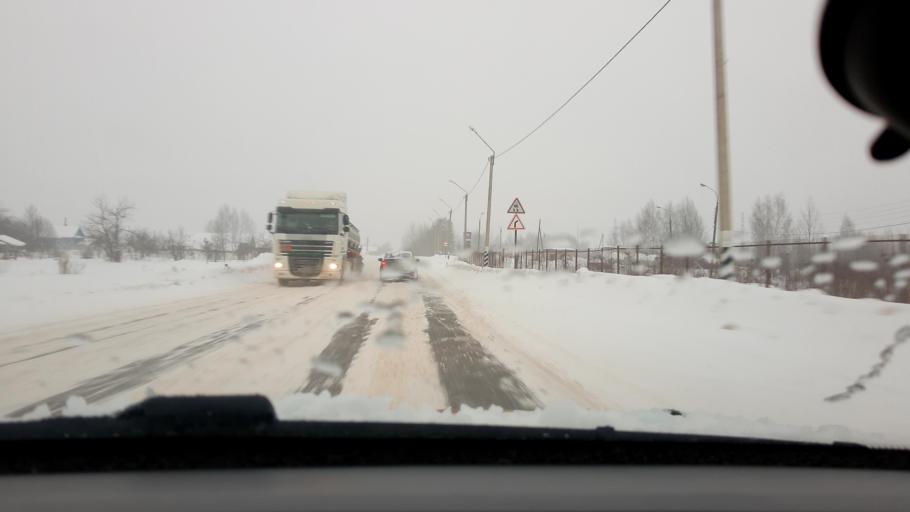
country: RU
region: Nizjnij Novgorod
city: Purekh
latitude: 56.6658
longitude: 43.1038
